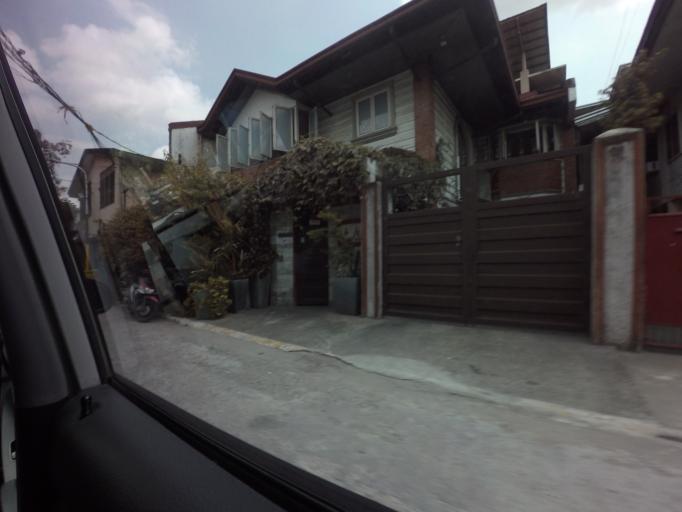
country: PH
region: Metro Manila
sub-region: San Juan
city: San Juan
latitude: 14.5931
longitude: 121.0195
